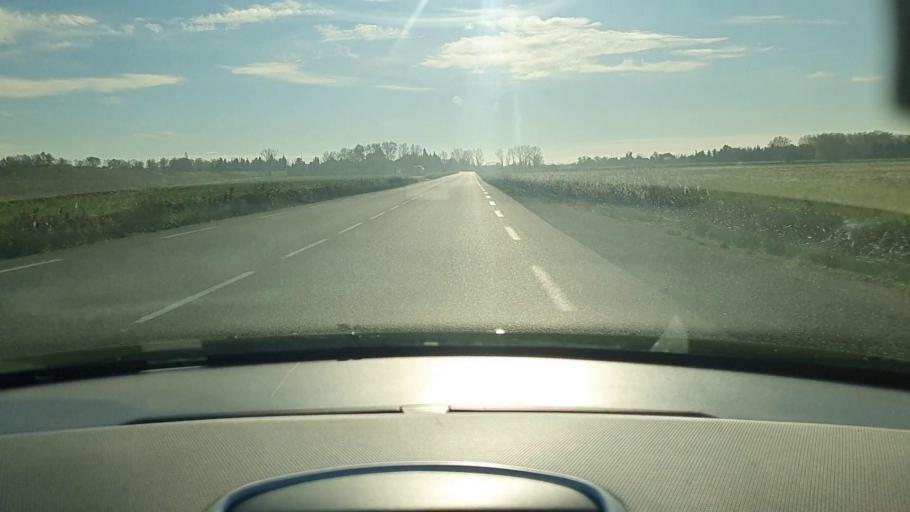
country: FR
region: Languedoc-Roussillon
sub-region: Departement du Gard
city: Fourques
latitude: 43.7445
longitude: 4.6127
